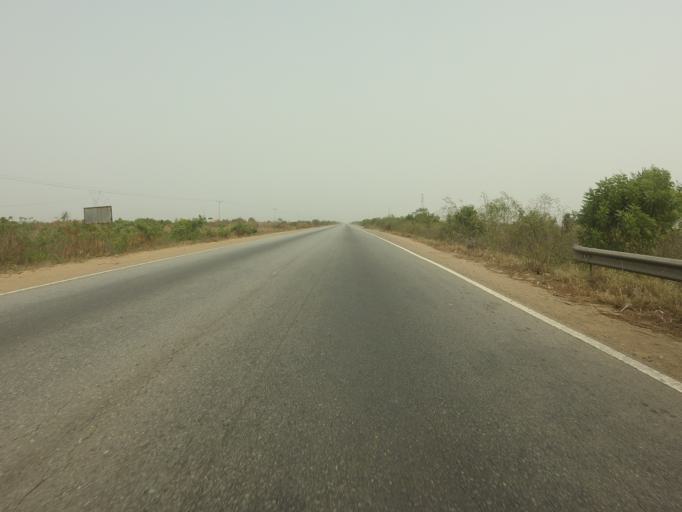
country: GH
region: Greater Accra
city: Tema
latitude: 5.7976
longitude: 0.1317
